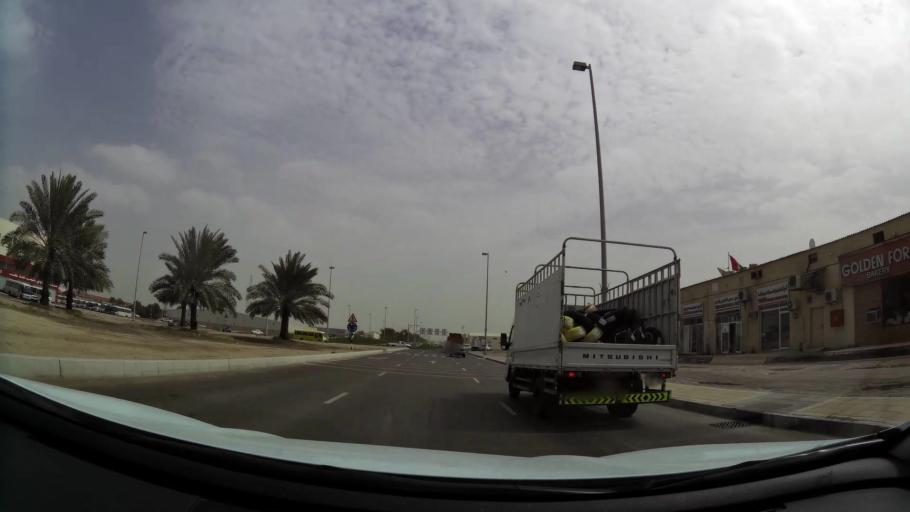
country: AE
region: Abu Dhabi
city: Abu Dhabi
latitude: 24.3723
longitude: 54.4900
